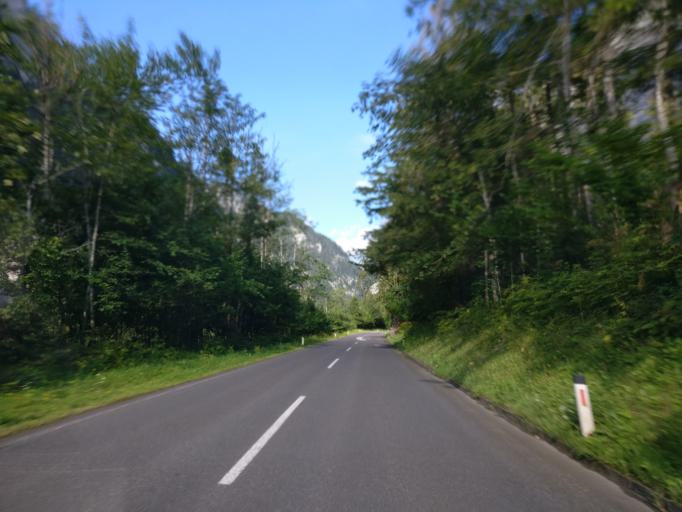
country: AT
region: Styria
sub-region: Politischer Bezirk Leoben
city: Hieflau
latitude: 47.5885
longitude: 14.6751
